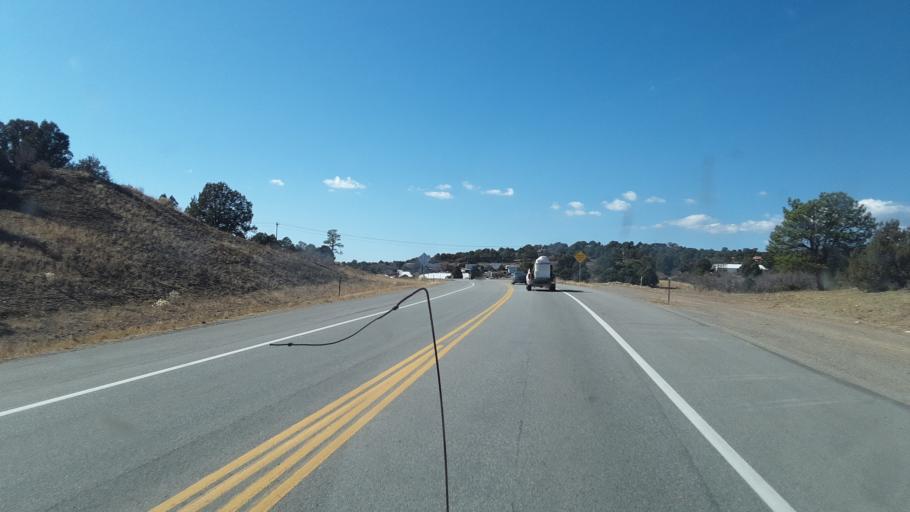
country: US
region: Colorado
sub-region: La Plata County
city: Bayfield
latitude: 37.2267
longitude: -107.6937
